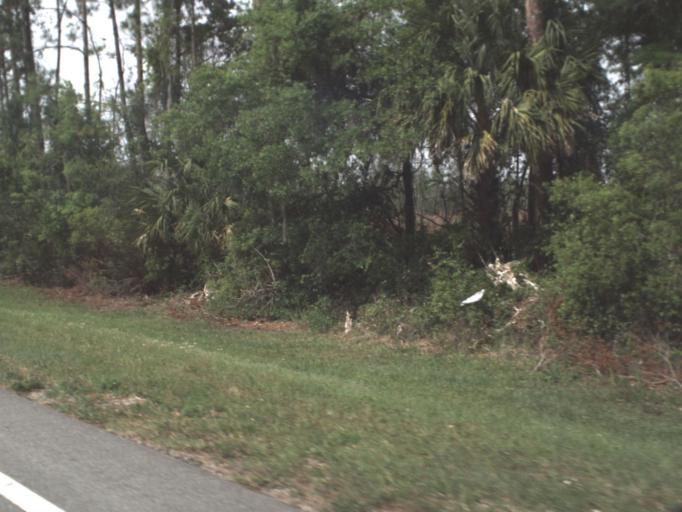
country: US
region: Florida
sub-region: Putnam County
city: Crescent City
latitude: 29.5297
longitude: -81.5140
